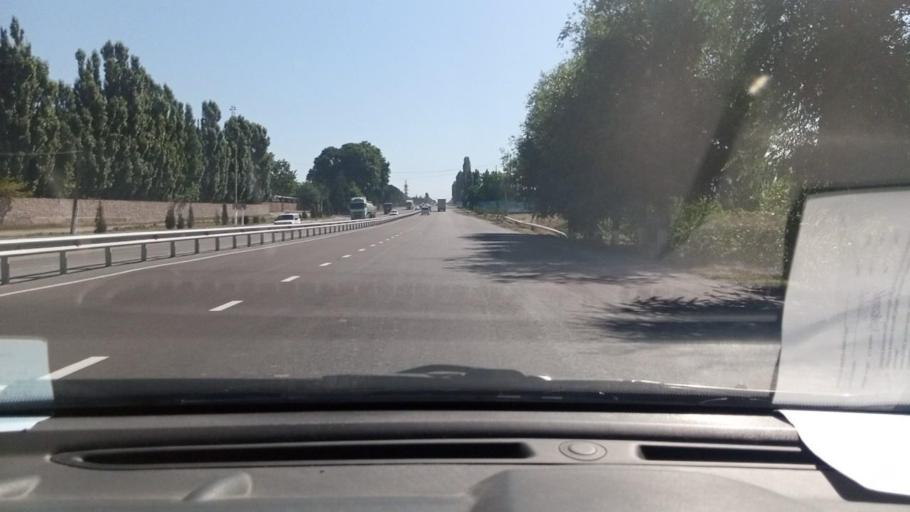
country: UZ
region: Toshkent
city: Angren
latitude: 40.9753
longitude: 70.0010
